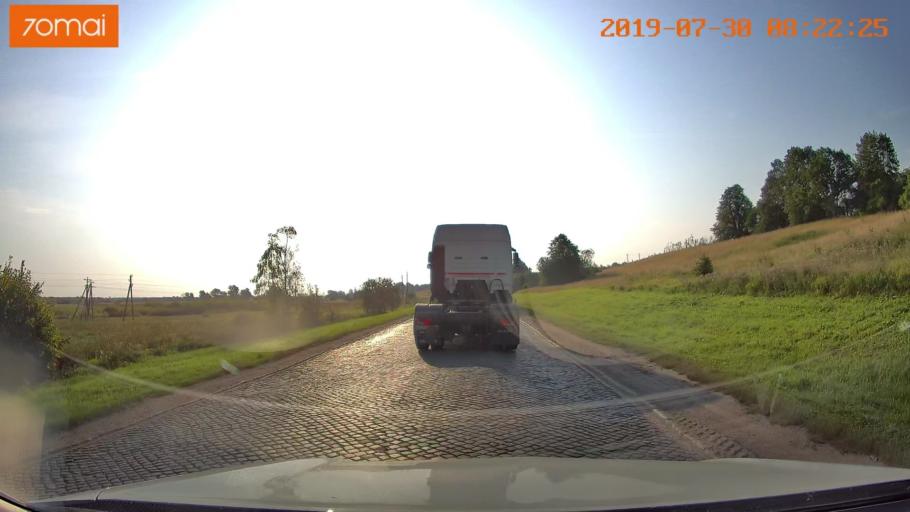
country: RU
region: Kaliningrad
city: Chernyakhovsk
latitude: 54.6255
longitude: 21.5337
